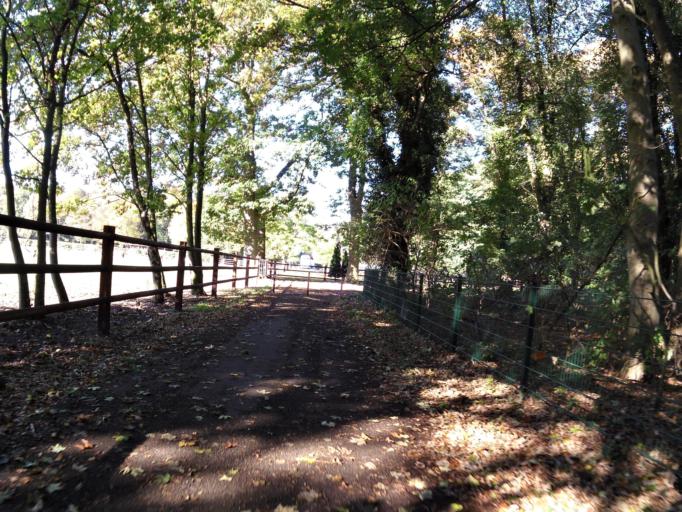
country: NL
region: Limburg
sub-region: Gemeente Venlo
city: Arcen
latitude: 51.5027
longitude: 6.2258
